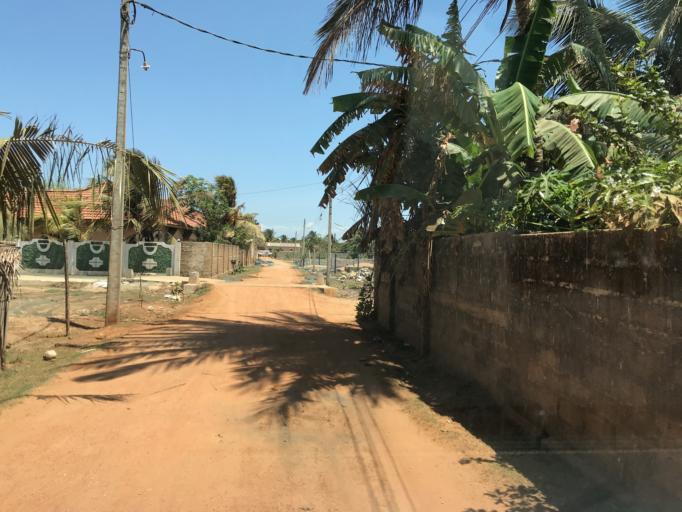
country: LK
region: Northern Province
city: Vavuniya
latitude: 8.9838
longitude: 79.9005
